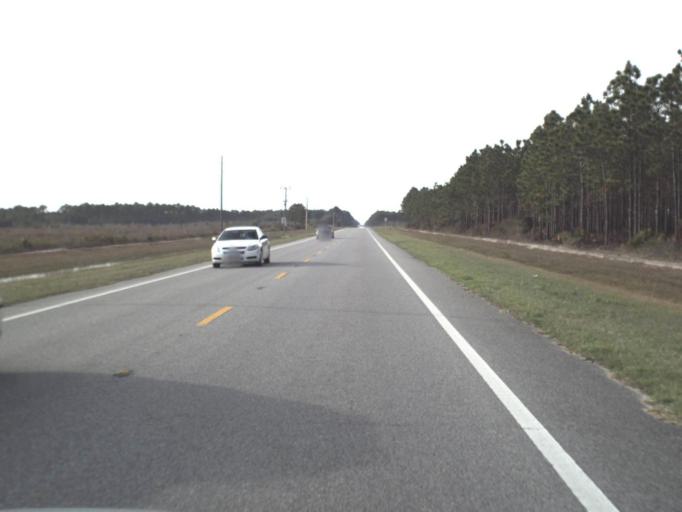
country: US
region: Florida
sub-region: Bay County
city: Tyndall Air Force Base
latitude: 30.0180
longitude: -85.5228
